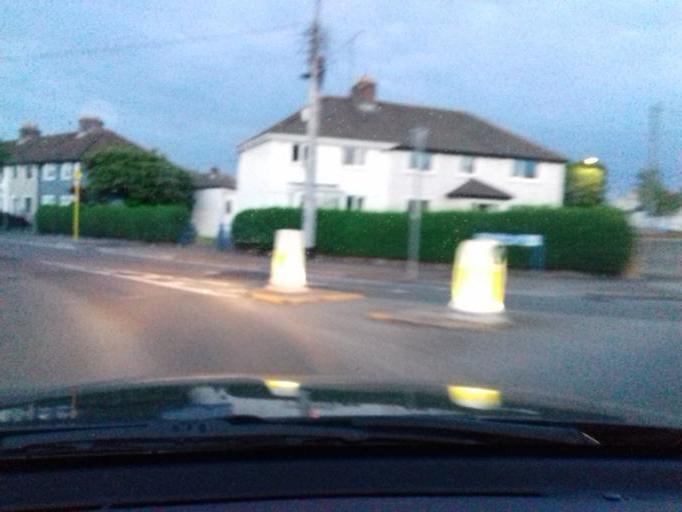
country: IE
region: Leinster
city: Crumlin
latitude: 53.3301
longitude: -6.3235
